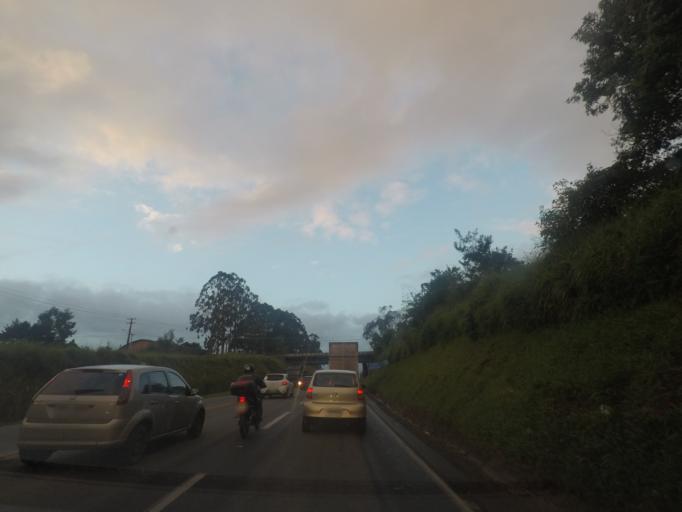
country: BR
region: Parana
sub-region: Curitiba
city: Curitiba
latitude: -25.4088
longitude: -49.3648
